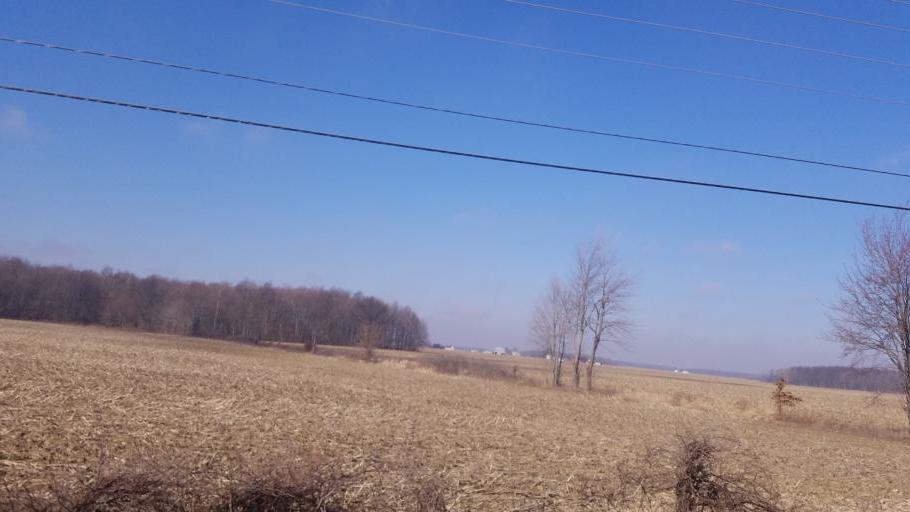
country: US
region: Ohio
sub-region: Huron County
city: Willard
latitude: 41.0161
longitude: -82.9116
